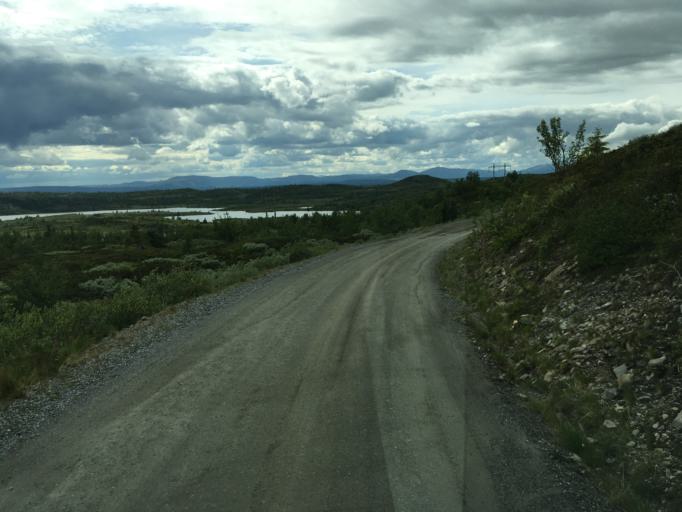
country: NO
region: Oppland
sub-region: Ringebu
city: Ringebu
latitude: 61.3634
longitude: 10.0340
